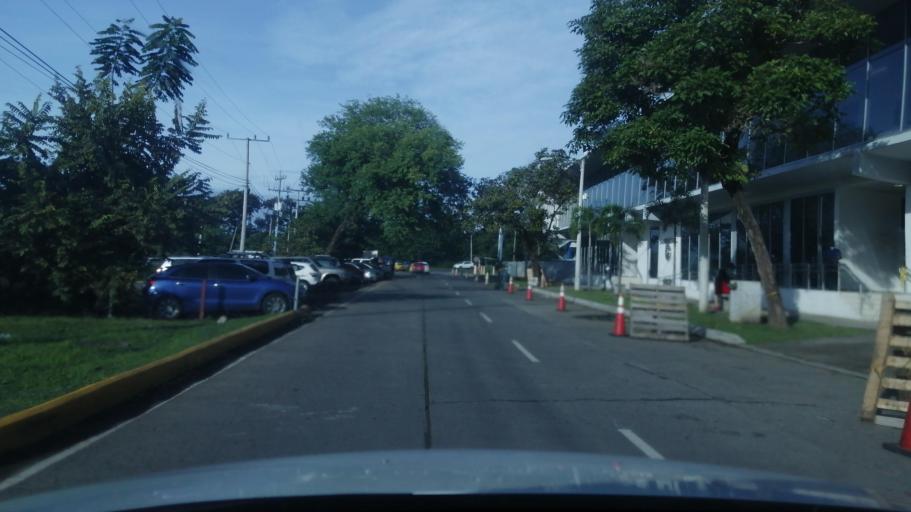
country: PA
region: Chiriqui
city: David
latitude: 8.4307
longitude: -82.4539
